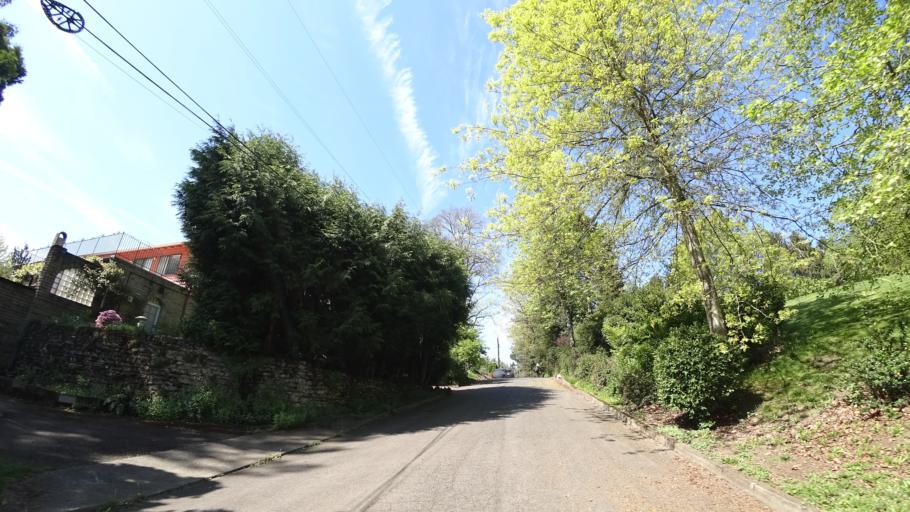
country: US
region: Oregon
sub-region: Clackamas County
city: Milwaukie
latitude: 45.4830
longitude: -122.6247
